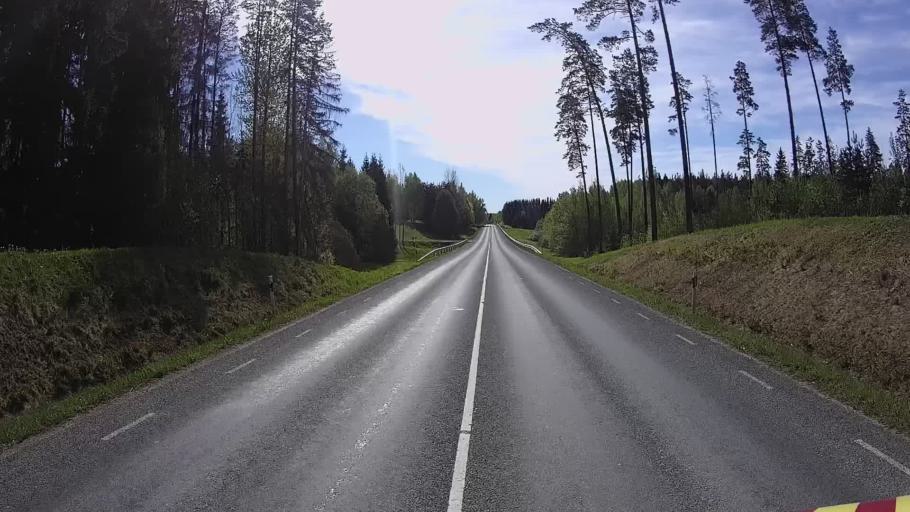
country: EE
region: Polvamaa
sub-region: Polva linn
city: Polva
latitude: 58.1622
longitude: 27.1573
